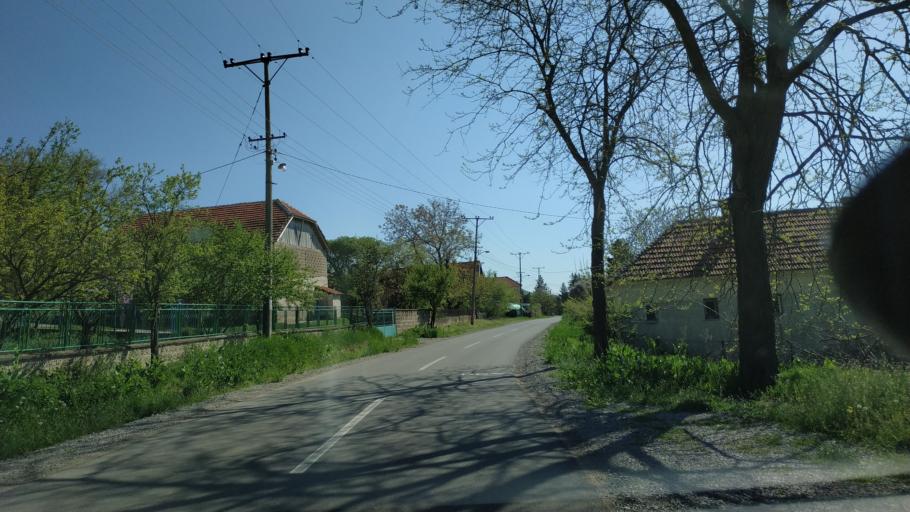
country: RS
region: Central Serbia
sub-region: Nisavski Okrug
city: Nis
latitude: 43.4490
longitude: 21.8482
